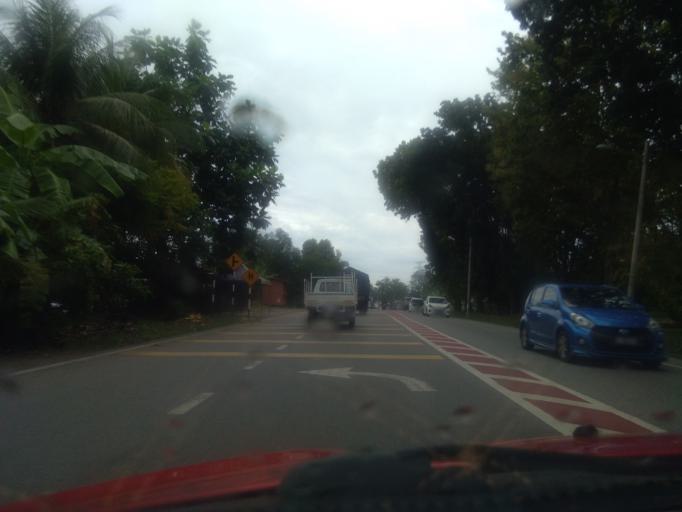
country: MY
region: Kedah
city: Sungai Petani
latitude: 5.6295
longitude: 100.5244
